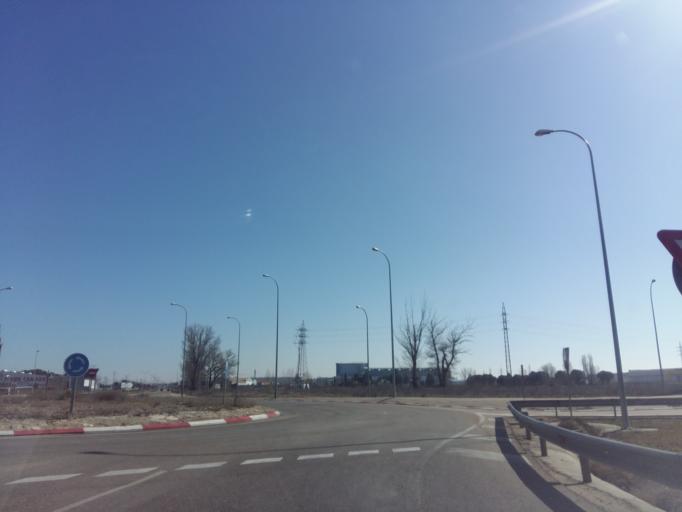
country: ES
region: Castille and Leon
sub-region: Provincia de Burgos
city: Villalba de Duero
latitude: 41.6645
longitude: -3.7281
